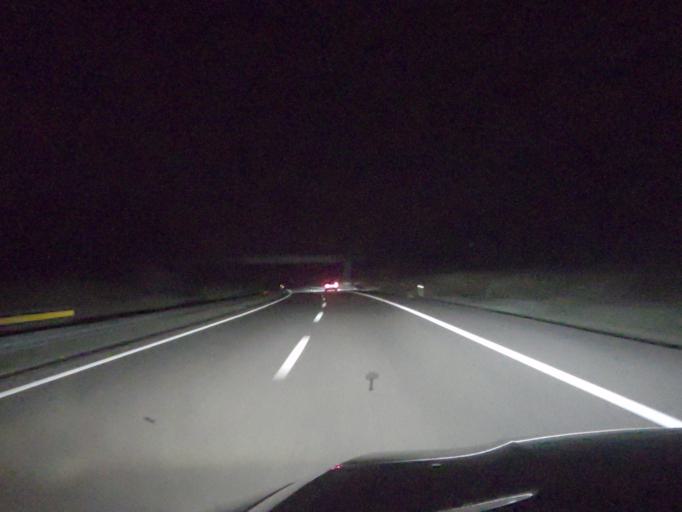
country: PT
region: Coimbra
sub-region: Condeixa-A-Nova
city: Condeixa-a-Nova
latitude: 40.1004
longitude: -8.5307
